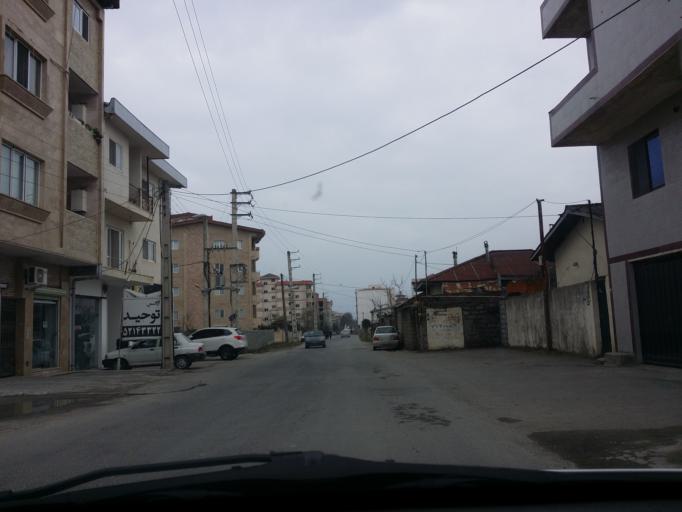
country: IR
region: Mazandaran
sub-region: Nowshahr
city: Nowshahr
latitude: 36.6471
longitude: 51.4835
